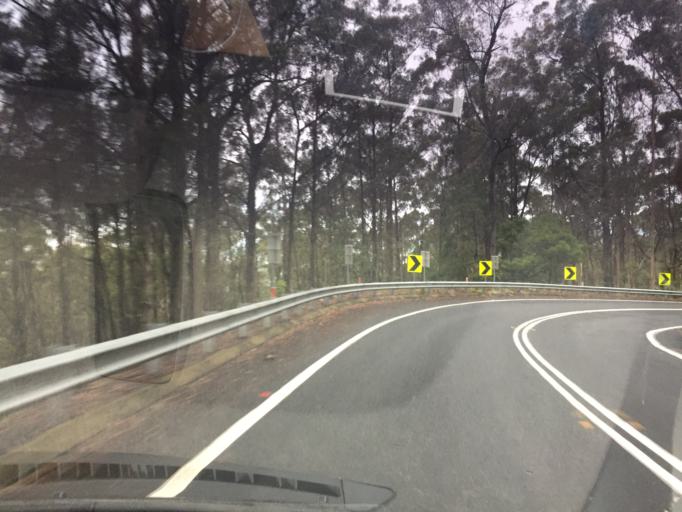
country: AU
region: New South Wales
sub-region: Bega Valley
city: Bega
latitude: -36.6078
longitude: 149.4691
